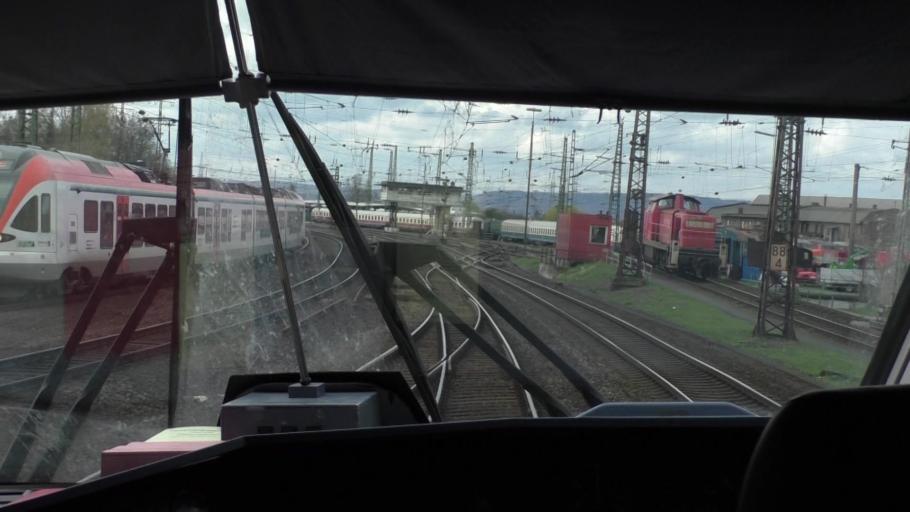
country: DE
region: Rheinland-Pfalz
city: Koblenz
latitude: 50.3788
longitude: 7.5873
